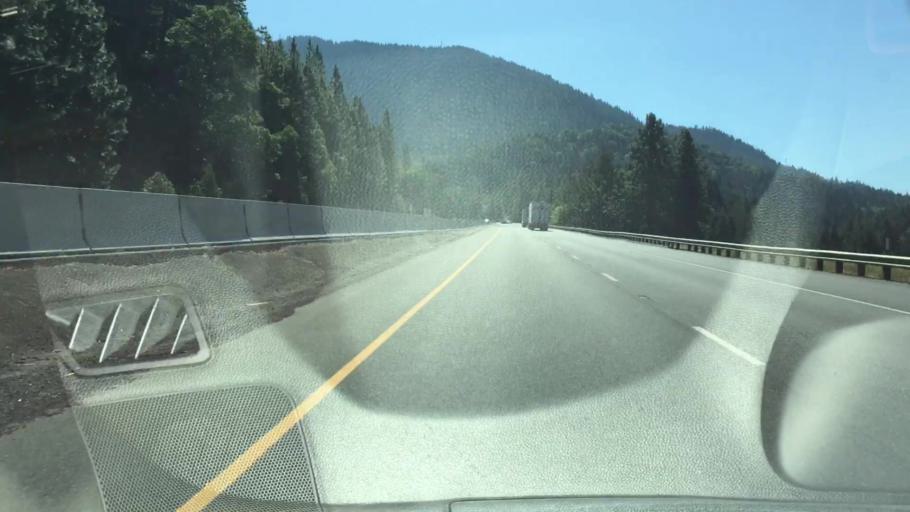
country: US
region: Oregon
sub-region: Josephine County
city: Merlin
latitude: 42.6232
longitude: -123.3842
